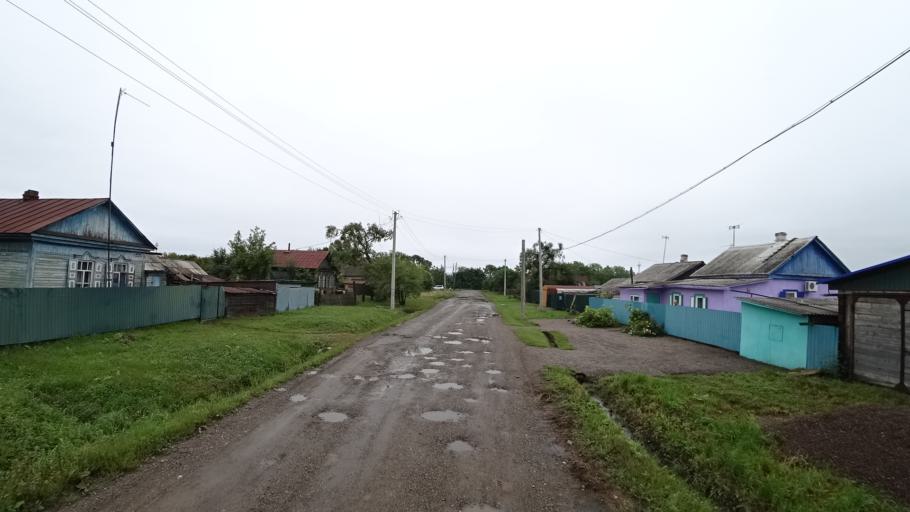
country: RU
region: Primorskiy
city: Monastyrishche
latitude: 44.2069
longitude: 132.4341
